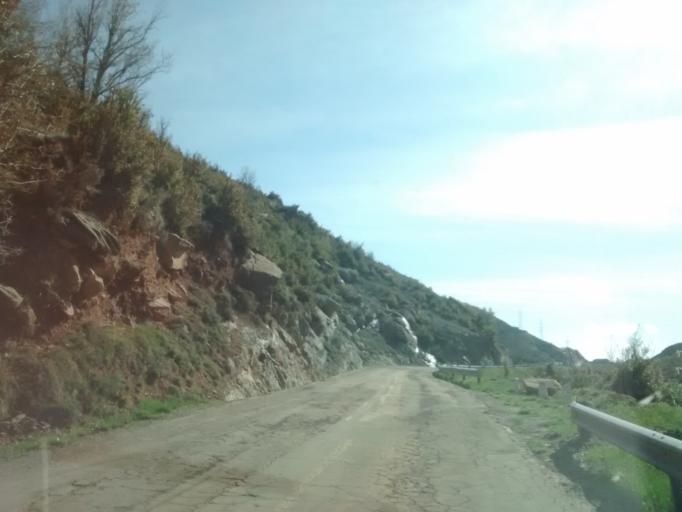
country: ES
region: Aragon
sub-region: Provincia de Huesca
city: Arguis
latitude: 42.3252
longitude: -0.4251
